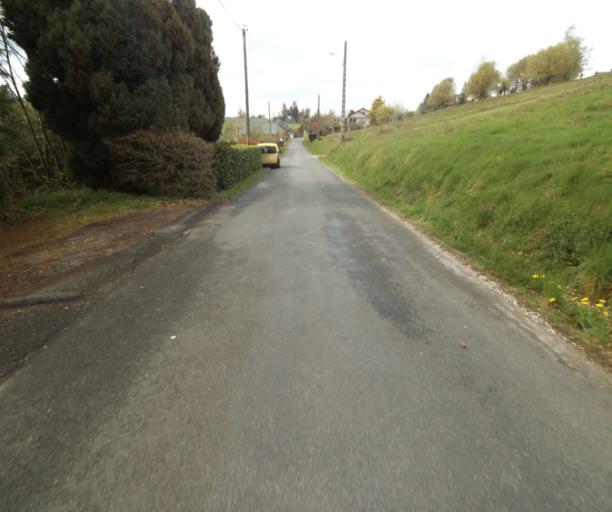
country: FR
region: Limousin
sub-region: Departement de la Correze
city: Tulle
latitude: 45.2754
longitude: 1.7492
